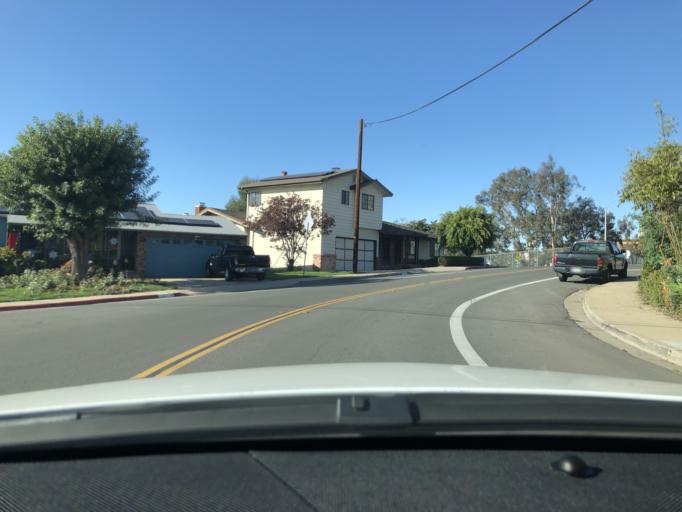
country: US
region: California
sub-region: San Diego County
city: Lemon Grove
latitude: 32.7543
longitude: -117.0727
